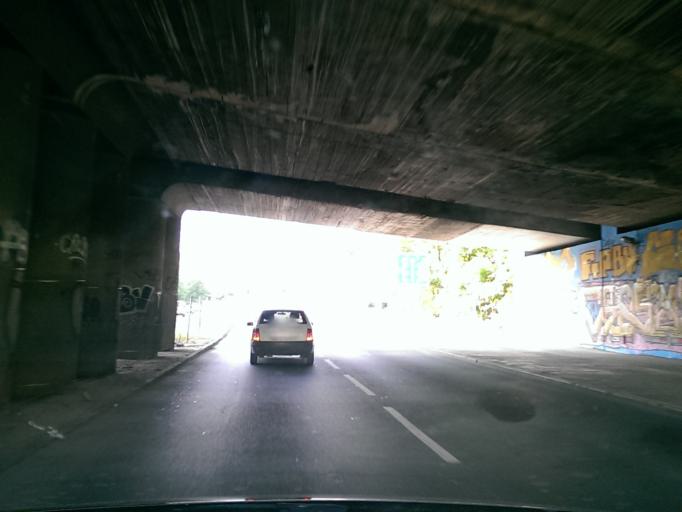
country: CZ
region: Praha
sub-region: Praha 4
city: Hodkovicky
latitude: 50.0357
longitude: 14.4560
